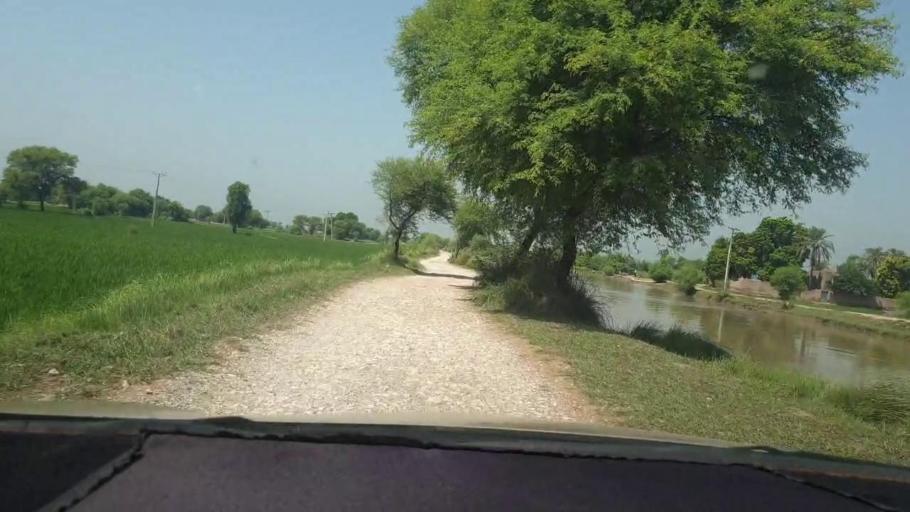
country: PK
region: Sindh
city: Kambar
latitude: 27.6073
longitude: 68.0805
